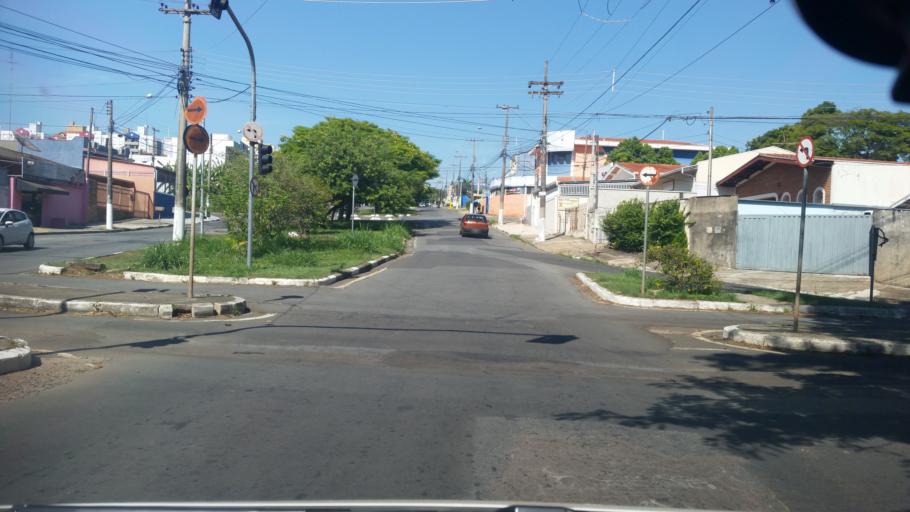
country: BR
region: Sao Paulo
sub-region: Campinas
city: Campinas
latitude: -22.8508
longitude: -47.0660
